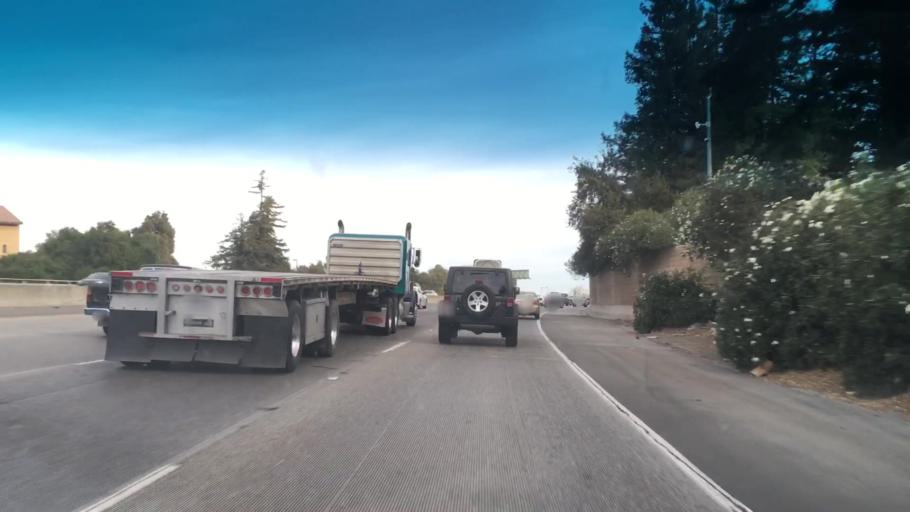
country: US
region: California
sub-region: Yolo County
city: West Sacramento
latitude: 38.5335
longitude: -121.5171
